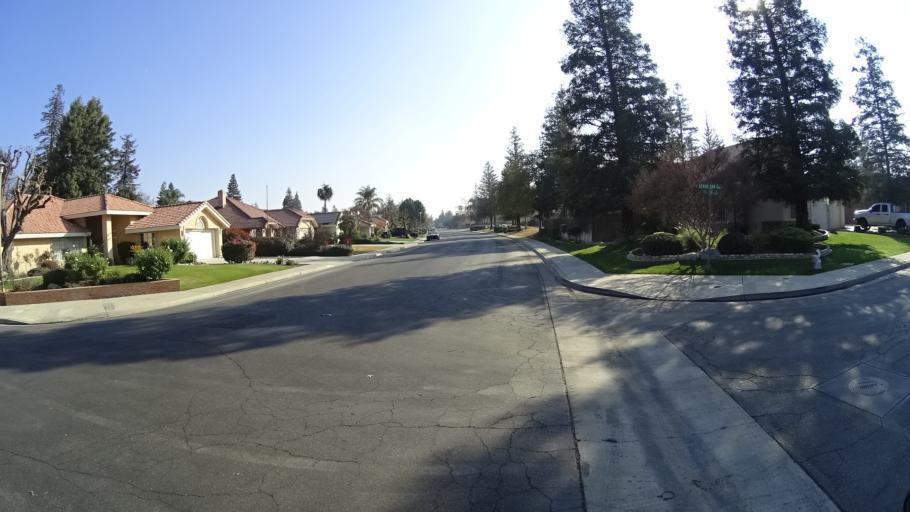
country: US
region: California
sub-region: Kern County
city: Greenacres
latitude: 35.3371
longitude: -119.1127
